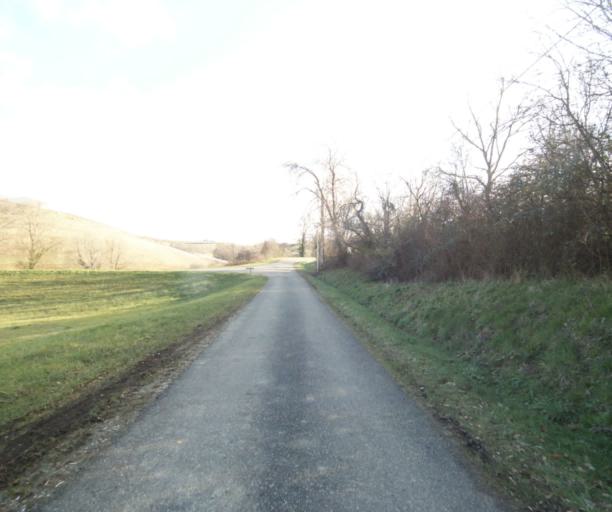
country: FR
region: Midi-Pyrenees
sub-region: Departement du Tarn-et-Garonne
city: Moissac
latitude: 44.1211
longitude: 1.0461
